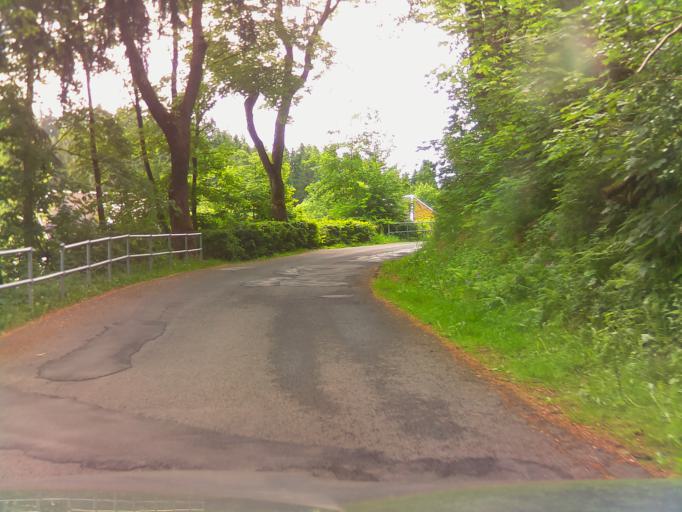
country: DE
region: Thuringia
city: Schmiedefeld am Rennsteig
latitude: 50.6061
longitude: 10.8161
